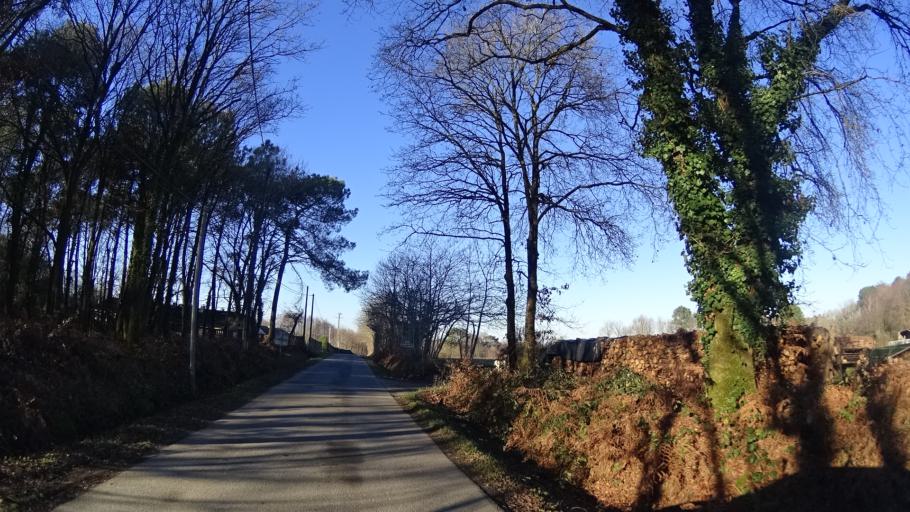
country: FR
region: Brittany
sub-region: Departement du Morbihan
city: Allaire
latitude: 47.6436
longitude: -2.1768
